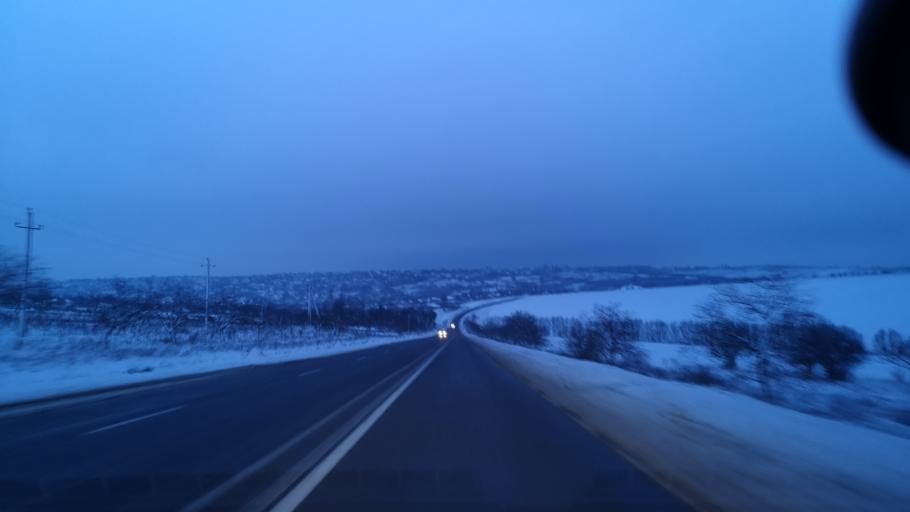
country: MD
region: Soldanesti
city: Soldanesti
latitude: 47.7118
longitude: 28.8473
